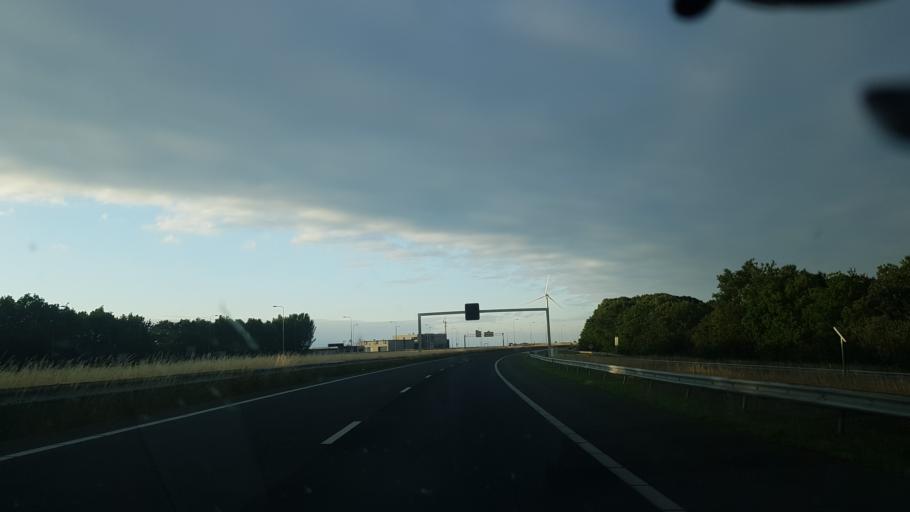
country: NL
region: North Holland
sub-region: Gemeente Hollands Kroon
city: Den Oever
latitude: 52.9300
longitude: 5.0365
